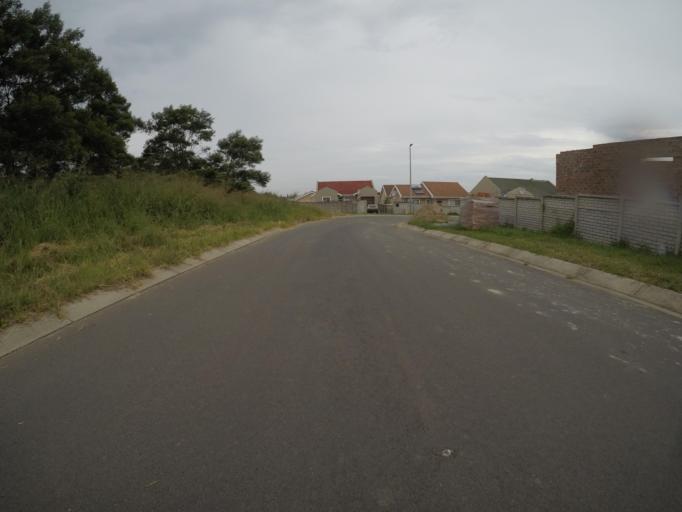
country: ZA
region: Eastern Cape
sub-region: Buffalo City Metropolitan Municipality
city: East London
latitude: -32.9962
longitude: 27.8538
